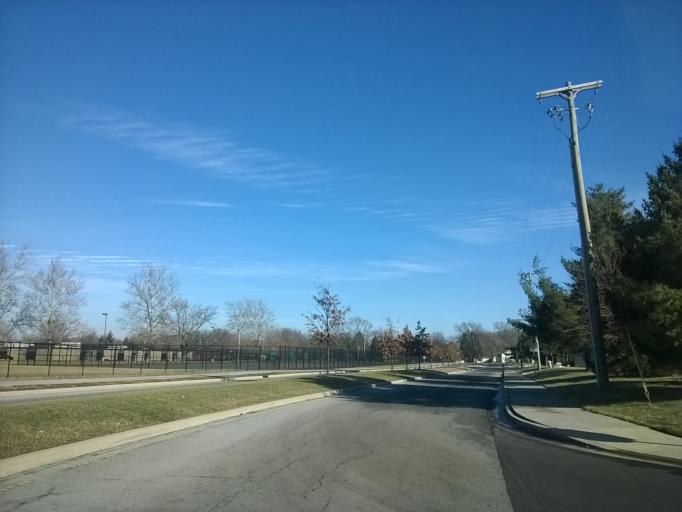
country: US
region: Indiana
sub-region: Hamilton County
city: Carmel
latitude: 39.9727
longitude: -86.1444
